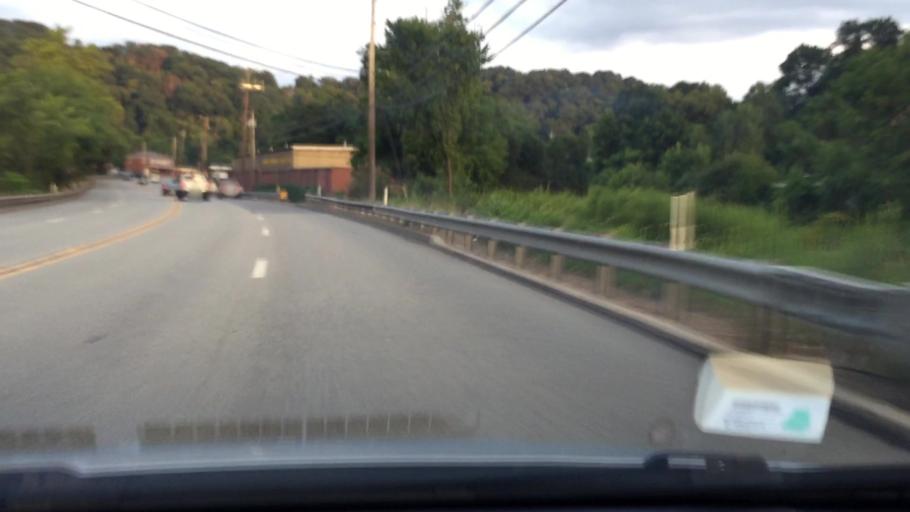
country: US
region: Pennsylvania
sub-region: Allegheny County
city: Glenshaw
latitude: 40.5262
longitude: -79.9497
